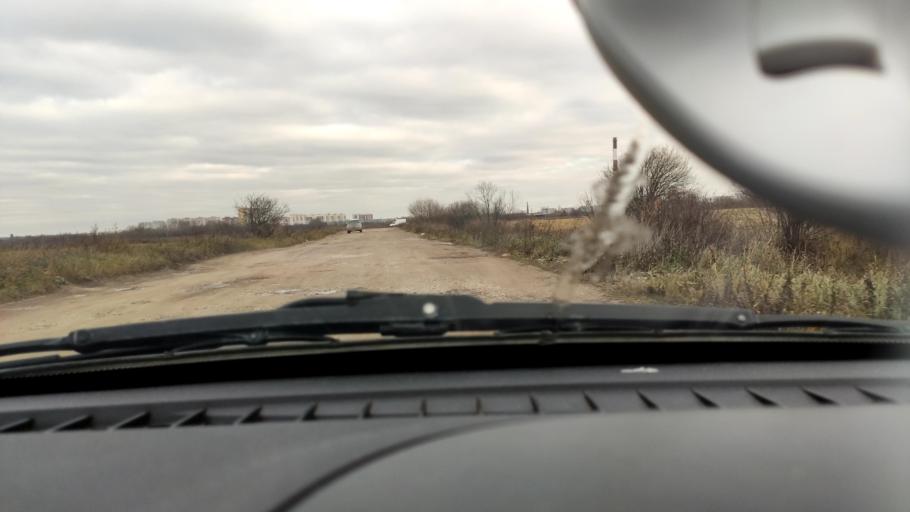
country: RU
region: Perm
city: Kondratovo
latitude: 57.9894
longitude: 56.0910
